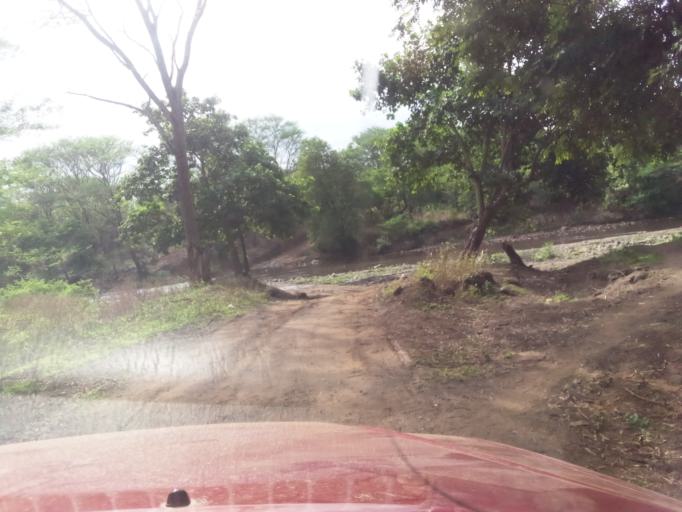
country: ET
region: Oromiya
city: Mendi
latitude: 10.0388
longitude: 35.3097
